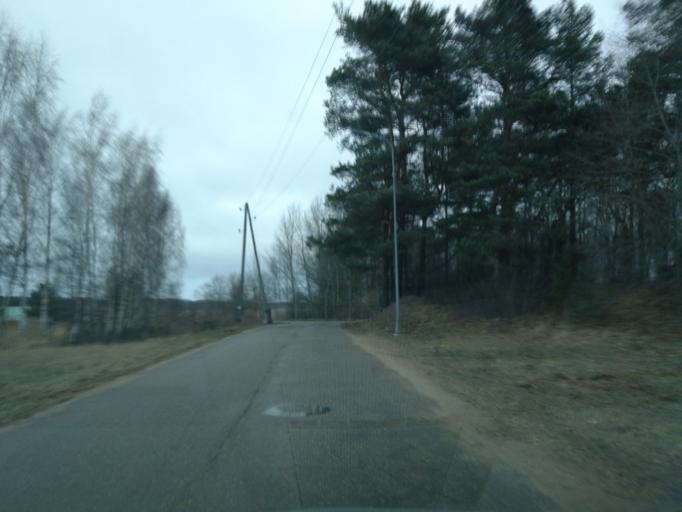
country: LV
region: Riga
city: Jaunciems
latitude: 57.0816
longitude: 24.1790
